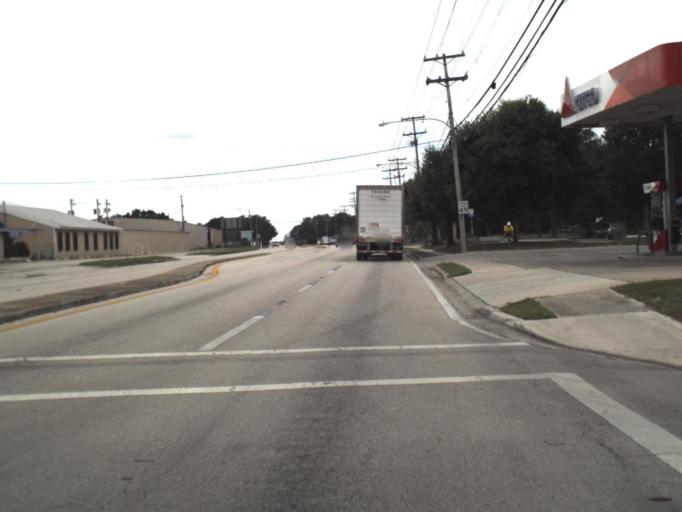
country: US
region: Florida
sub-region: Polk County
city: Bartow
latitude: 27.8824
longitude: -81.8286
